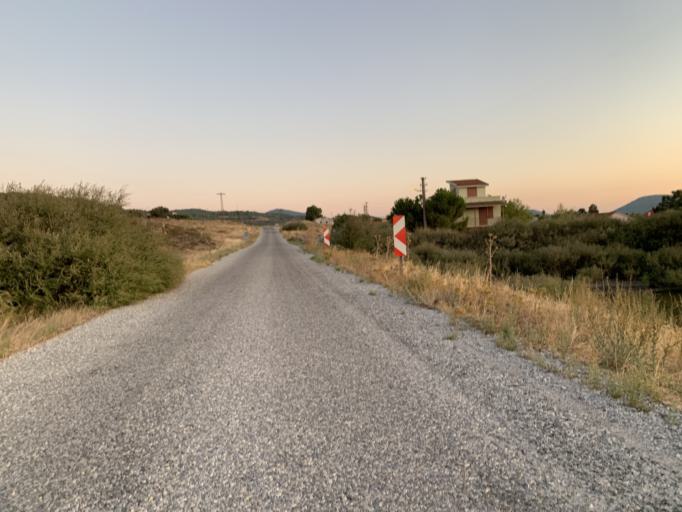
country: TR
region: Izmir
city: Uzunkuyu
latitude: 38.3260
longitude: 26.5836
